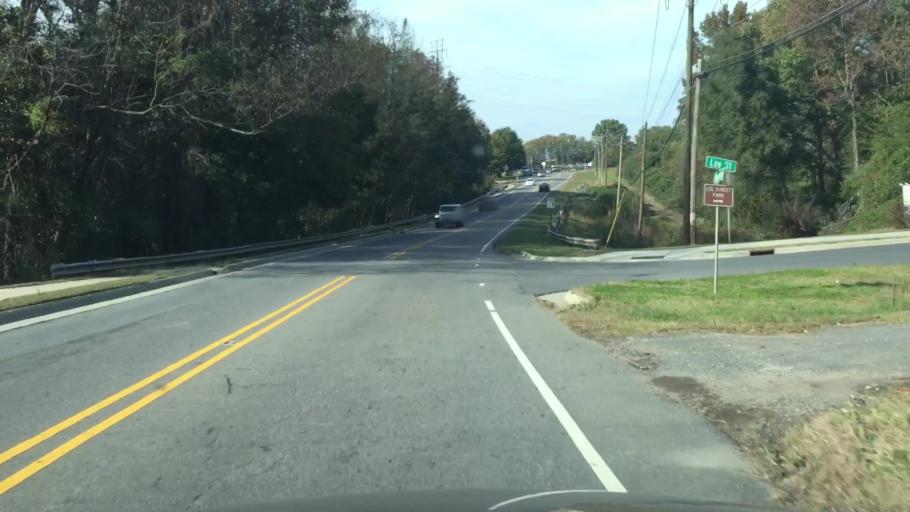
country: US
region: North Carolina
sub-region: Iredell County
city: Mooresville
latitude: 35.5915
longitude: -80.8154
